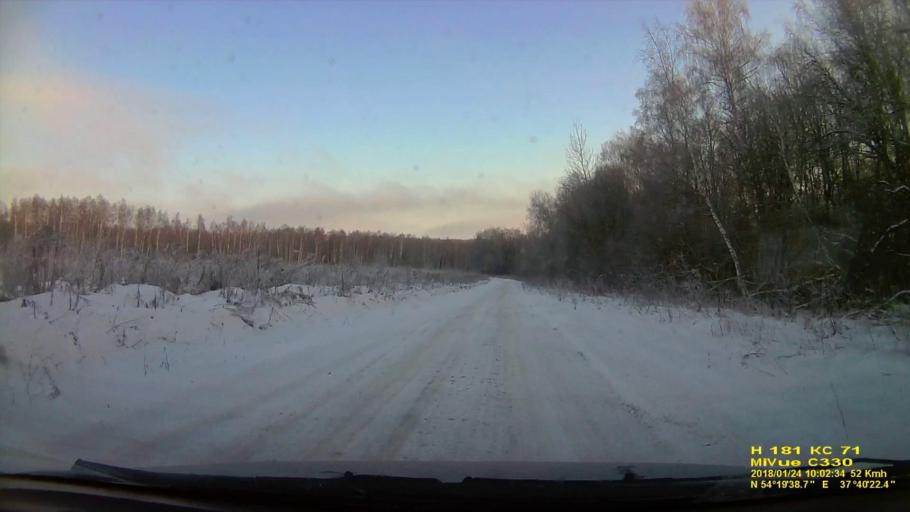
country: RU
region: Tula
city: Revyakino
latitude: 54.3275
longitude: 37.6730
